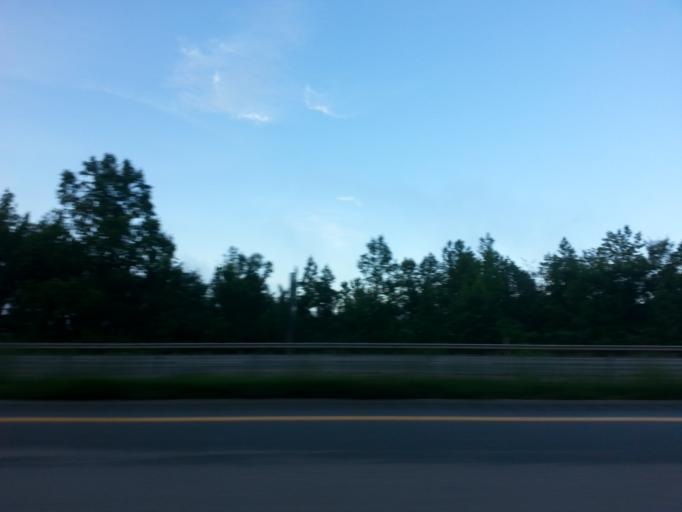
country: US
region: Kentucky
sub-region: Whitley County
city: Williamsburg
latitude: 36.6980
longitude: -84.1432
